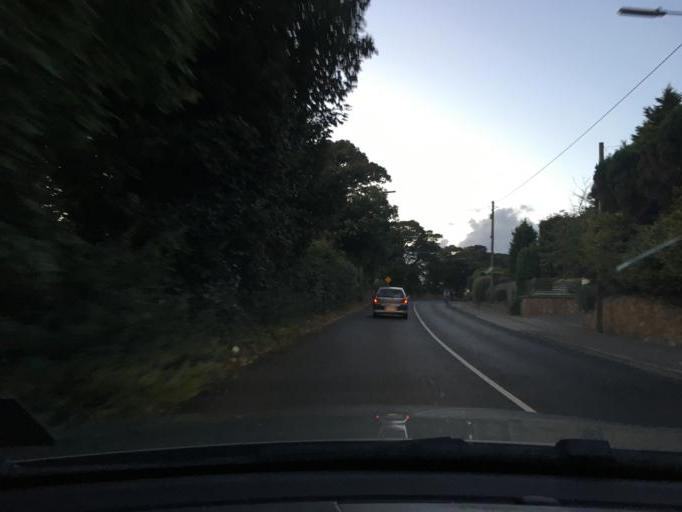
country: IE
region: Leinster
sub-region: Fingal County
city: Howth
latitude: 53.3700
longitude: -6.0854
